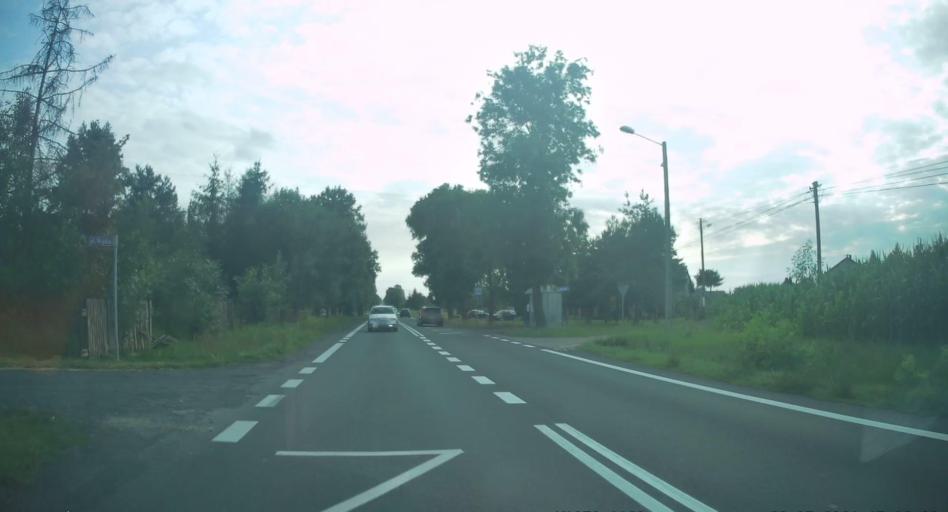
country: PL
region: Silesian Voivodeship
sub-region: Powiat czestochowski
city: Borowno
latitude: 50.9011
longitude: 19.2874
